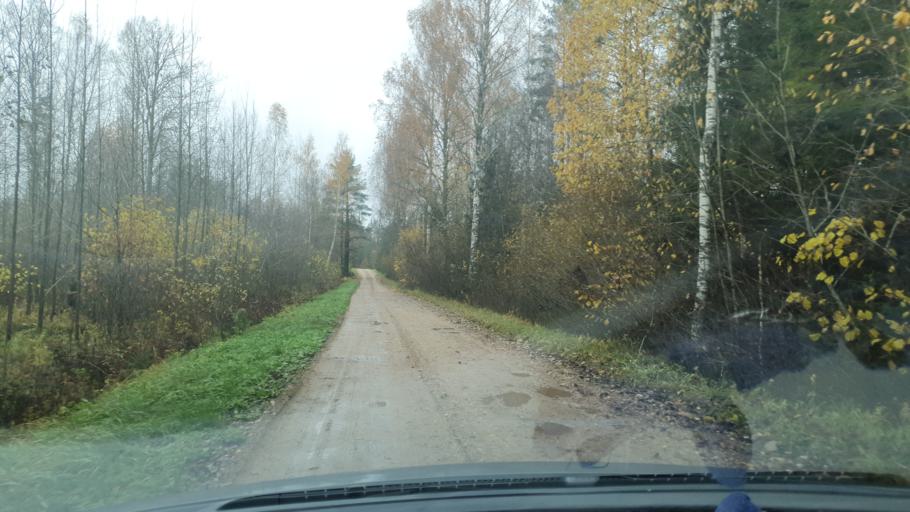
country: EE
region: Viljandimaa
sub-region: Karksi vald
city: Karksi-Nuia
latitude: 57.9901
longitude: 25.6402
